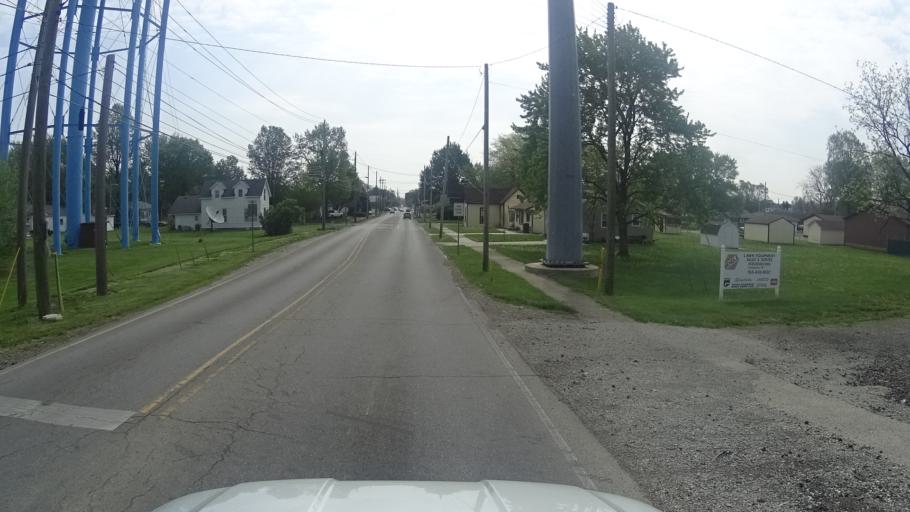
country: US
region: Indiana
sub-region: Madison County
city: Anderson
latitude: 40.1352
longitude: -85.6816
